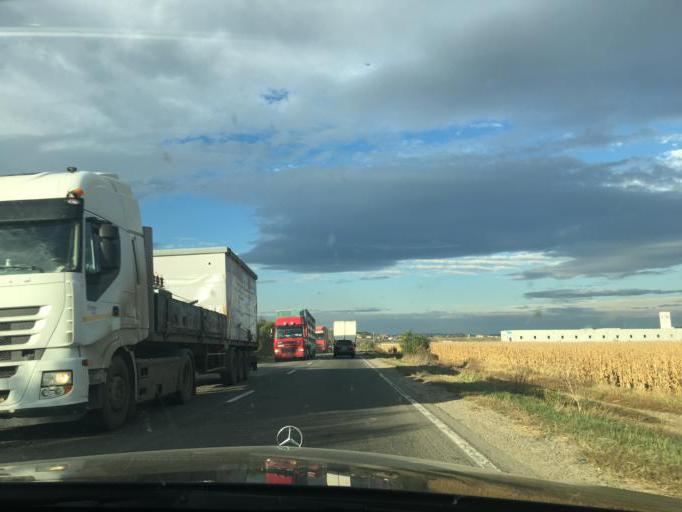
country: RO
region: Alba
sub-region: Oras Teius
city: Teius
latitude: 46.1854
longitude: 23.6599
